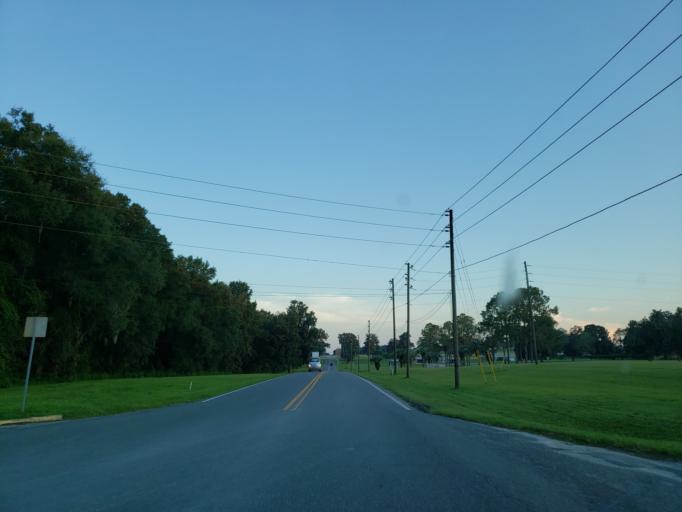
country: US
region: Florida
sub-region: Marion County
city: Citra
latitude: 29.3182
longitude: -82.1959
